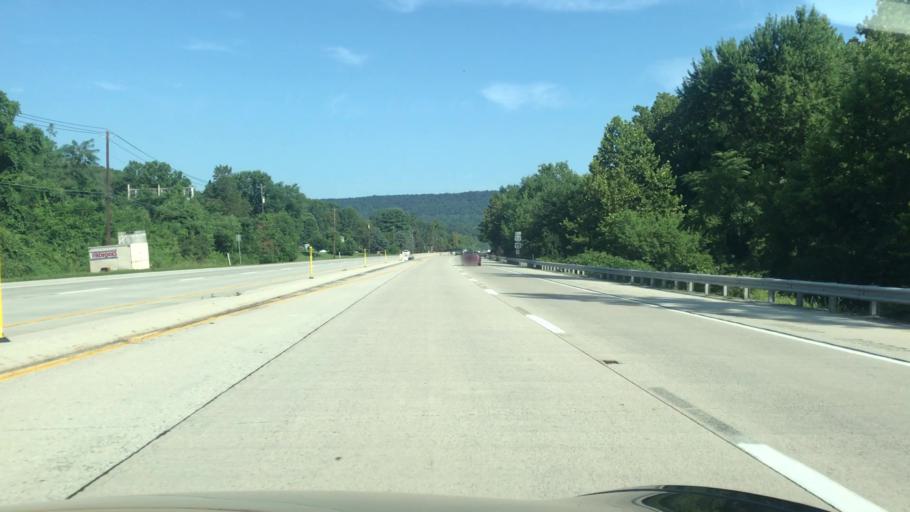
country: US
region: Pennsylvania
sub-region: Dauphin County
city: Millersburg
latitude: 40.4972
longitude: -76.9691
